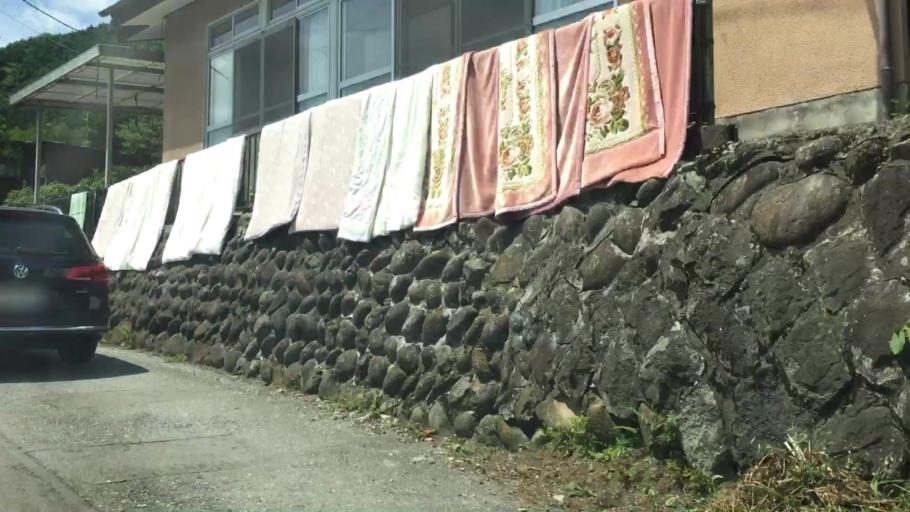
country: JP
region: Tochigi
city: Imaichi
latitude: 36.8478
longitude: 139.7266
